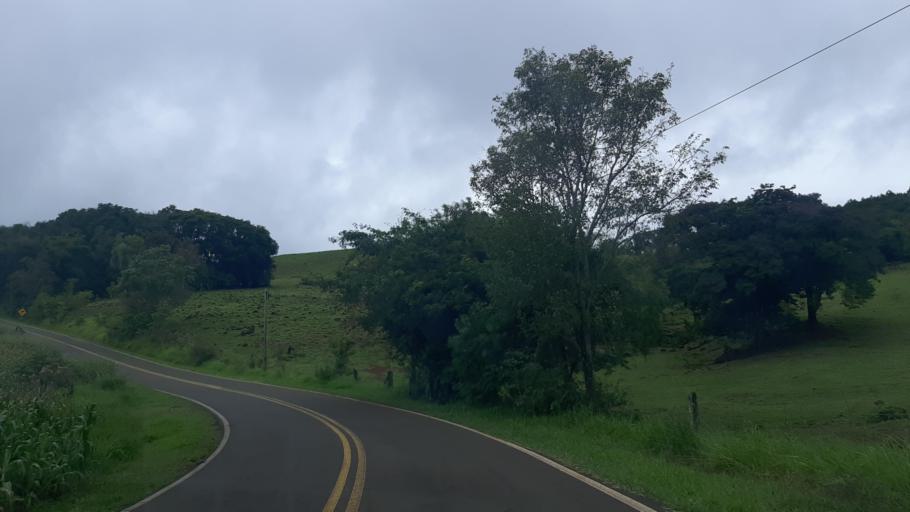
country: BR
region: Parana
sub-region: Ampere
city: Ampere
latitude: -25.9837
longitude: -53.4442
